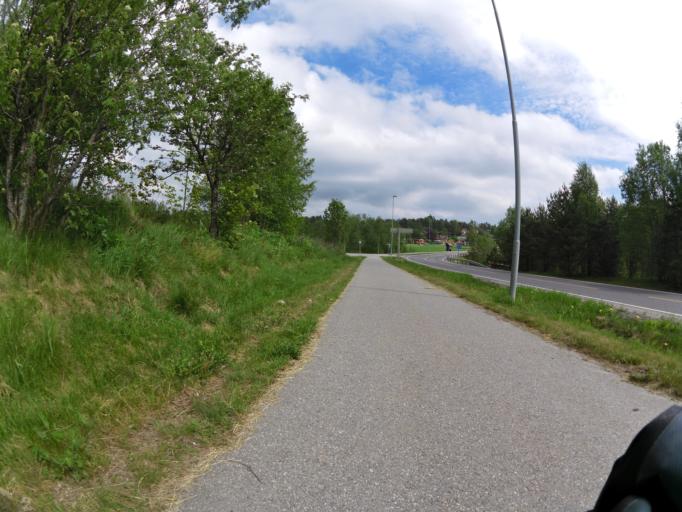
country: NO
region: Ostfold
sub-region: Rade
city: Karlshus
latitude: 59.3459
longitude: 10.9275
